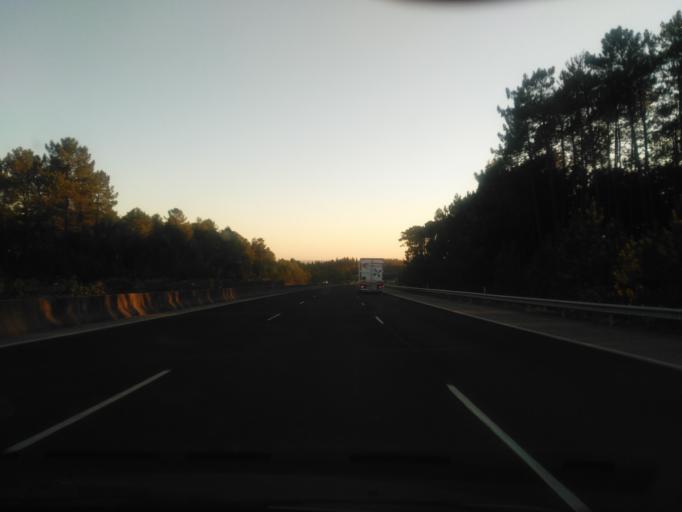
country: PT
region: Leiria
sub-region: Leiria
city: Maceira
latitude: 39.6807
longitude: -8.9378
